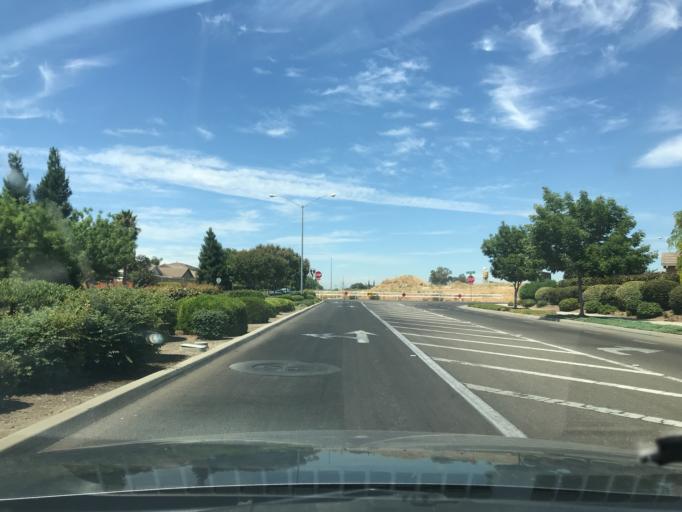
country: US
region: California
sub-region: Merced County
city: Merced
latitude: 37.3320
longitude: -120.4981
